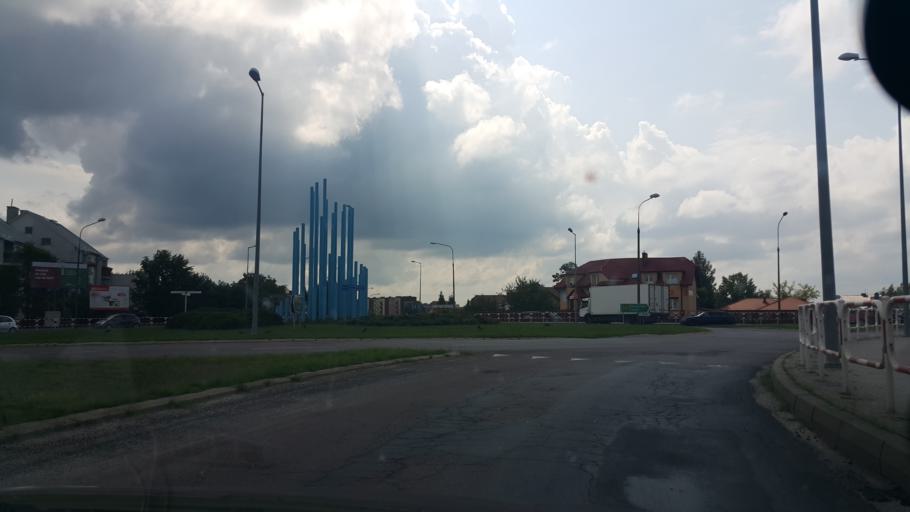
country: PL
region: Lublin Voivodeship
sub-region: Powiat wlodawski
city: Wlodawa
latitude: 51.5471
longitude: 23.5434
